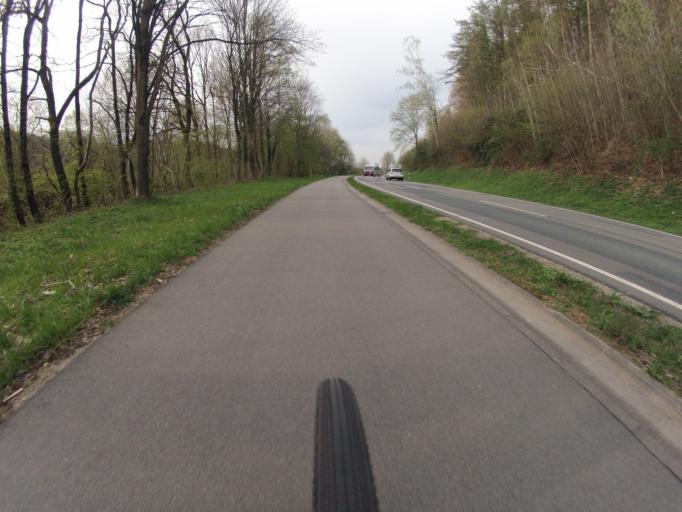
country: DE
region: North Rhine-Westphalia
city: Ibbenburen
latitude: 52.2375
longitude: 7.7414
